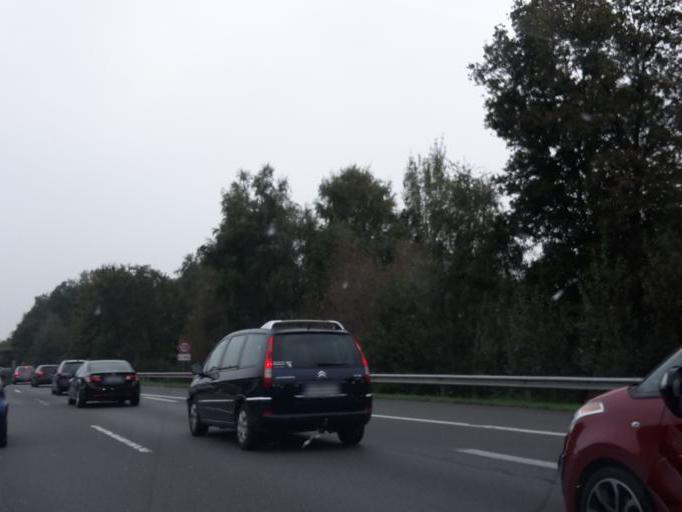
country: DE
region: Lower Saxony
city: Holdorf
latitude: 52.5957
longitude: 8.1129
